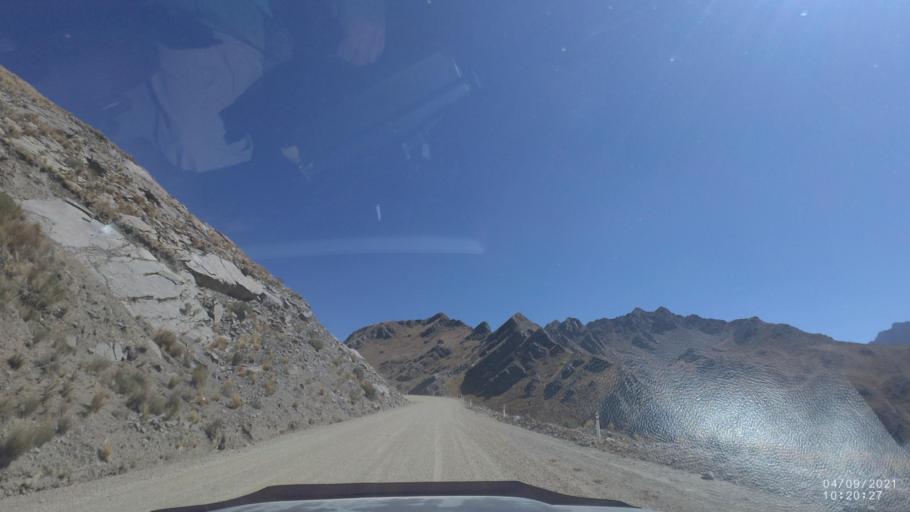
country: BO
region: Cochabamba
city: Sipe Sipe
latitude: -17.3142
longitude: -66.4280
